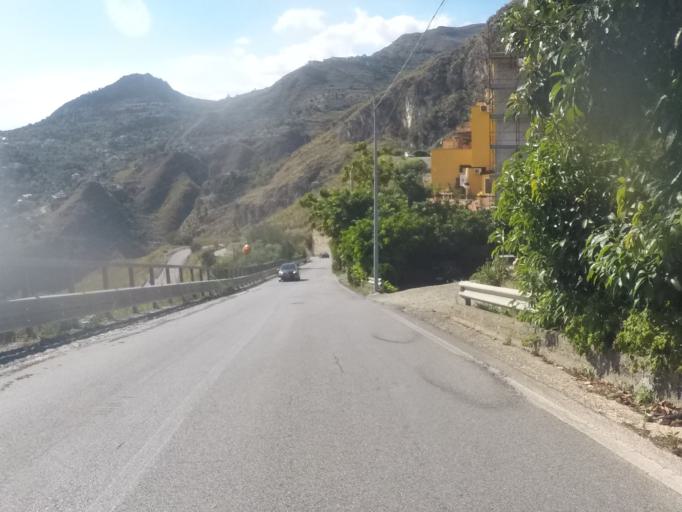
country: IT
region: Sicily
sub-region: Messina
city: Castelmola
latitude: 37.8543
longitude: 15.2786
